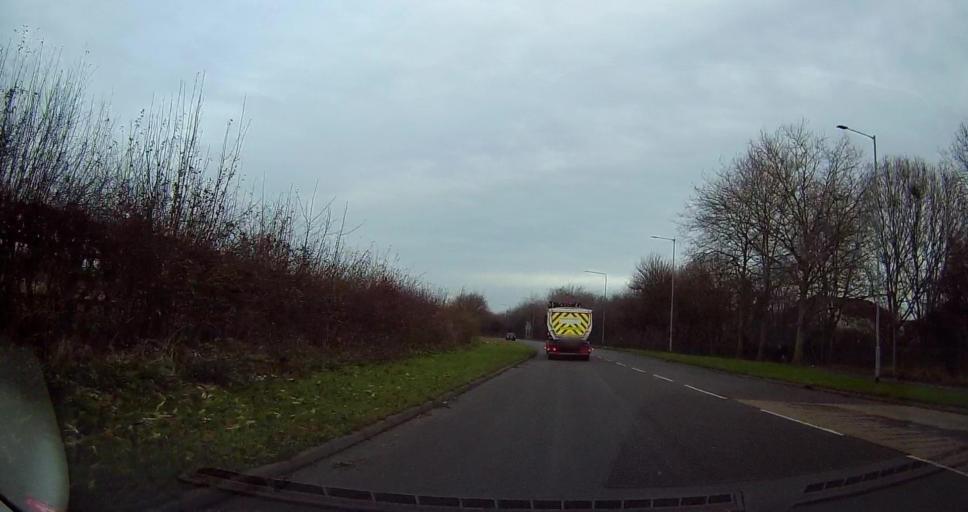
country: GB
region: England
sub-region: Nottinghamshire
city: Kimberley
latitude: 52.9681
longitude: -1.2363
